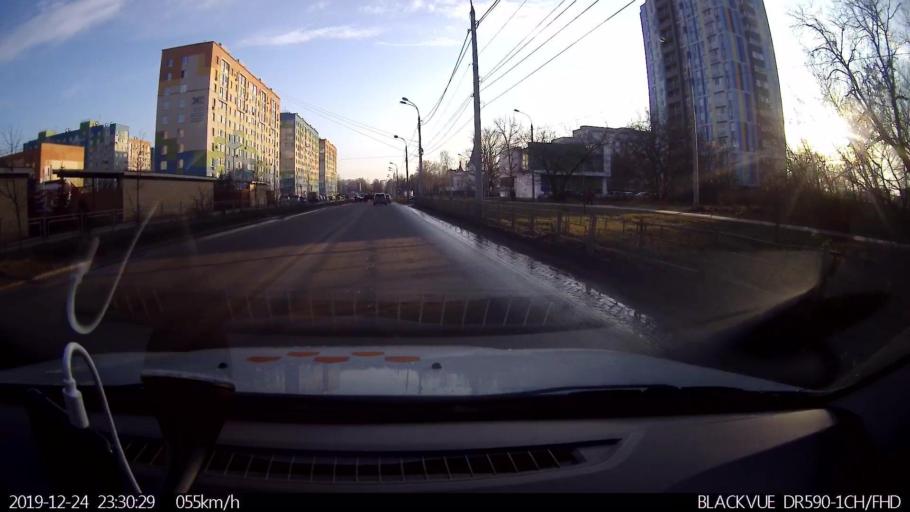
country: RU
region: Nizjnij Novgorod
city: Gorbatovka
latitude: 56.2350
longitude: 43.8425
